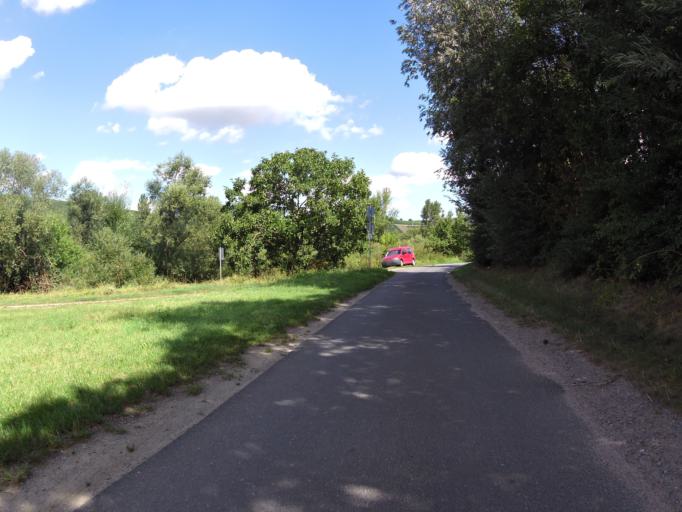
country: DE
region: Bavaria
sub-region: Regierungsbezirk Unterfranken
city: Nordheim
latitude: 49.8545
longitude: 10.1743
